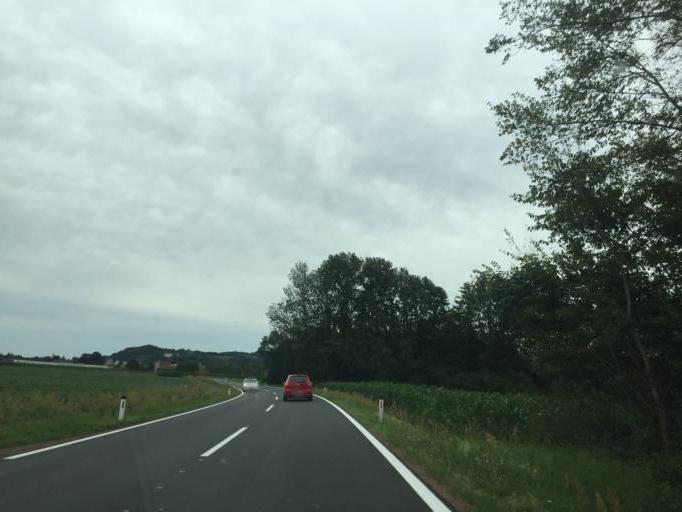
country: AT
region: Styria
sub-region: Politischer Bezirk Suedoststeiermark
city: Mureck
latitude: 46.7079
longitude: 15.7523
